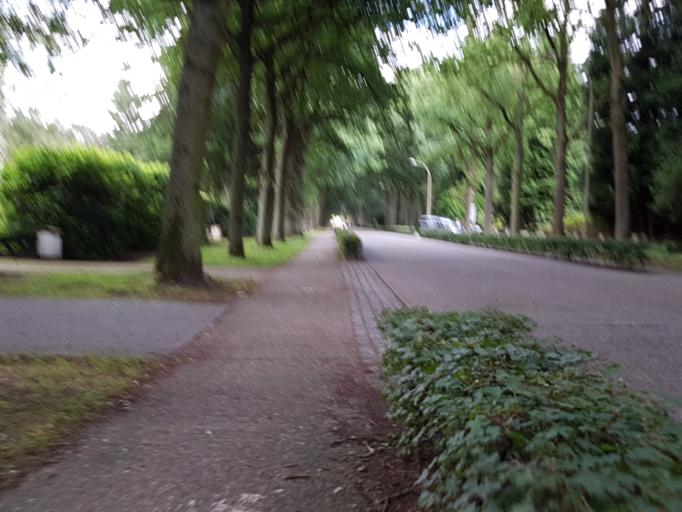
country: BE
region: Flanders
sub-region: Provincie Antwerpen
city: Kalmthout
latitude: 51.3672
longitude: 4.4487
